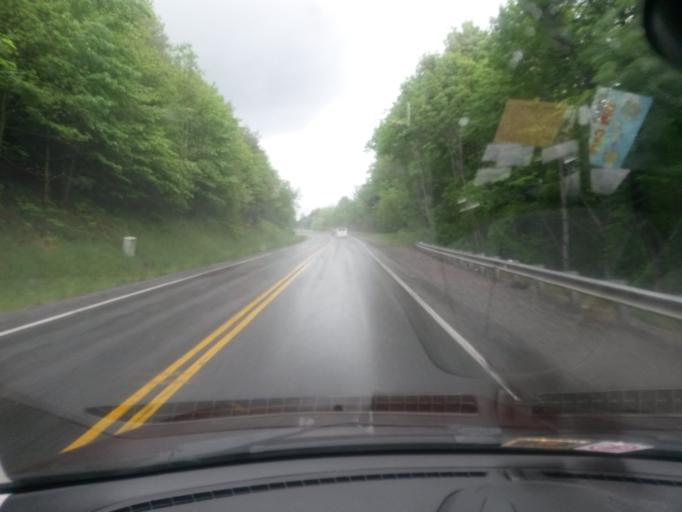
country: US
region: Virginia
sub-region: Floyd County
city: Floyd
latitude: 36.9685
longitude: -80.3826
